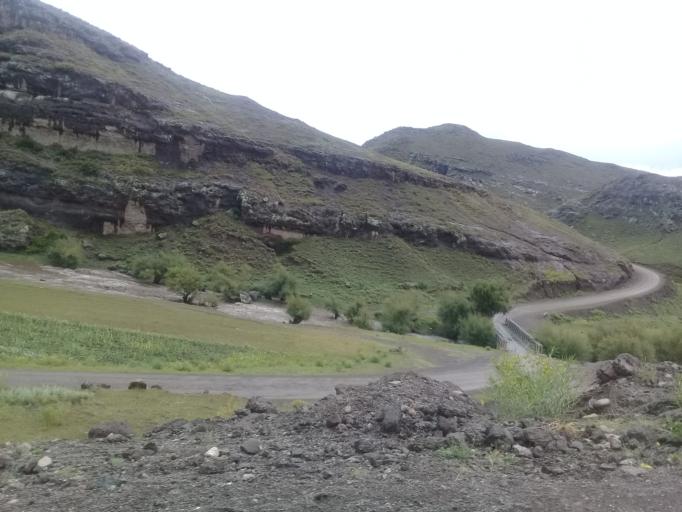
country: LS
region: Mokhotlong
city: Mokhotlong
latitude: -29.3345
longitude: 29.0267
